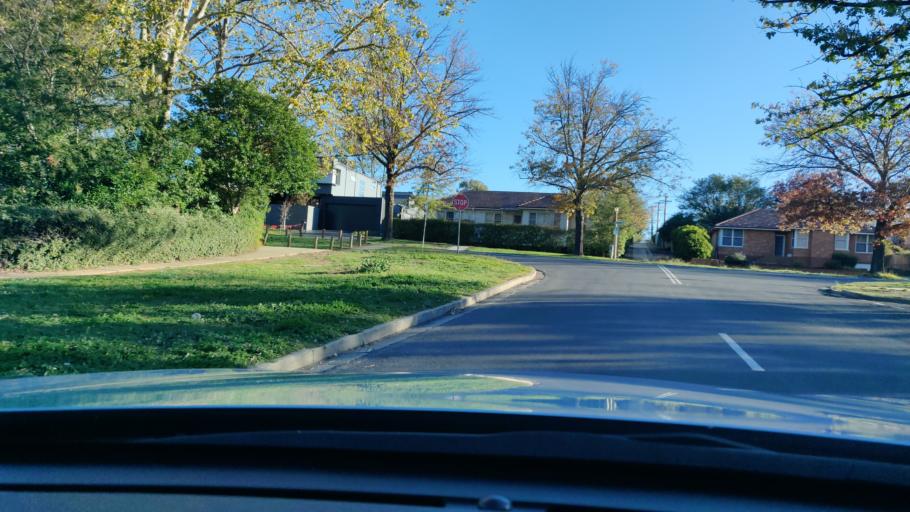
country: AU
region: Australian Capital Territory
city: Forrest
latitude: -35.3288
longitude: 149.1427
